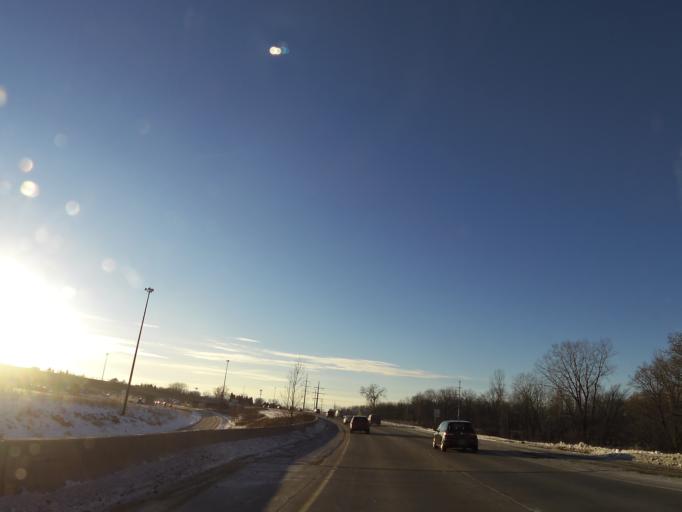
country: US
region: Minnesota
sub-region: Hennepin County
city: Eden Prairie
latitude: 44.8623
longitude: -93.4703
